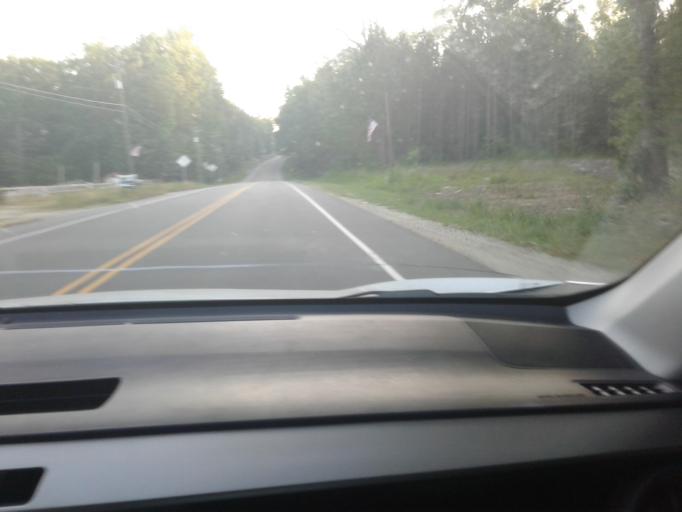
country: US
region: North Carolina
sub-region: Wake County
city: Fuquay-Varina
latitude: 35.5148
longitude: -78.8133
